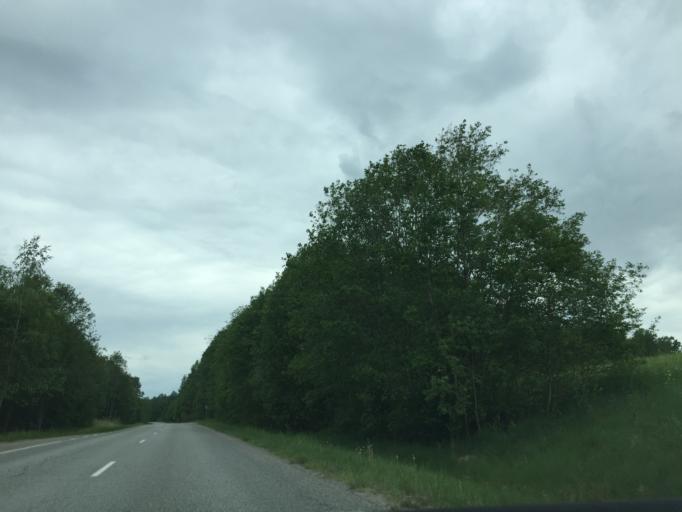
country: LV
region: Aglona
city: Aglona
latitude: 56.1389
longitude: 27.0985
